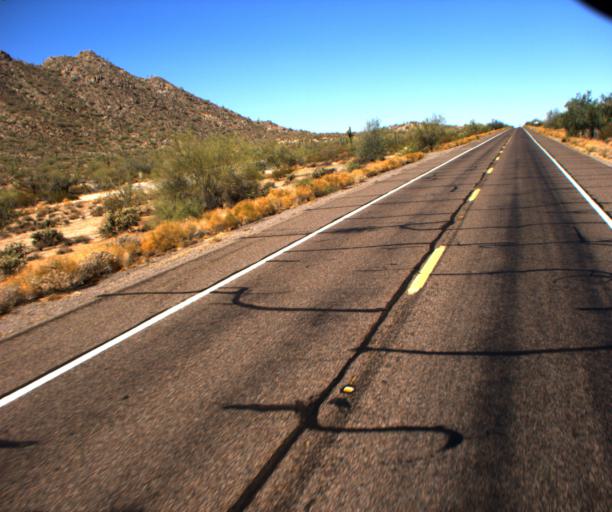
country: US
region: Arizona
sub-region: Pinal County
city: Sacaton
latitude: 33.0141
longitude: -111.6793
